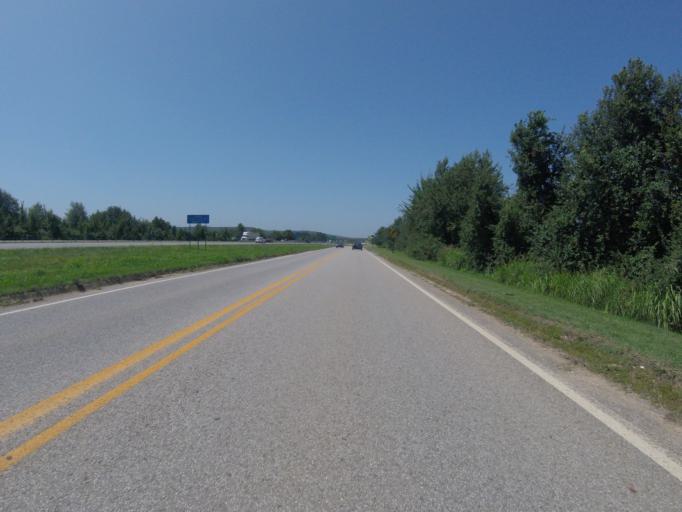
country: US
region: Arkansas
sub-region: Washington County
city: Johnson
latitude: 36.0958
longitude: -94.1887
